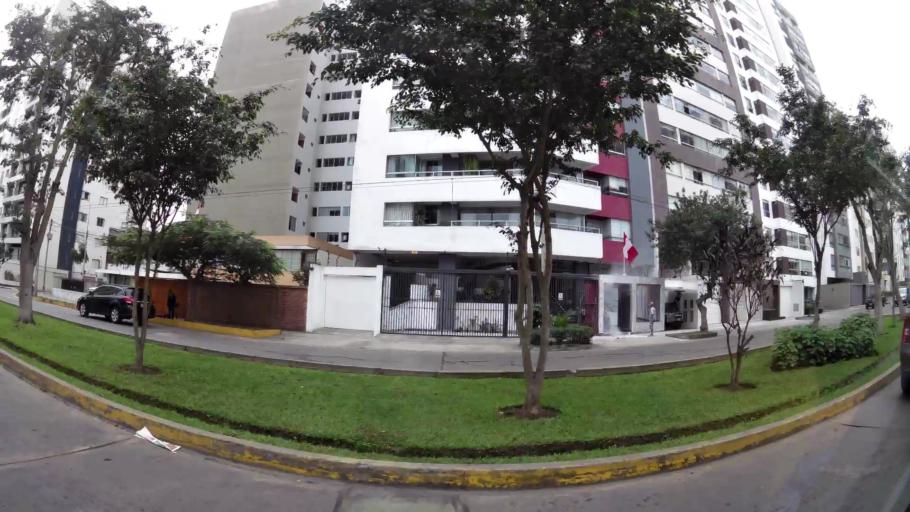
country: PE
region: Lima
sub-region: Lima
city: Surco
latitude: -12.1187
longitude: -77.0160
